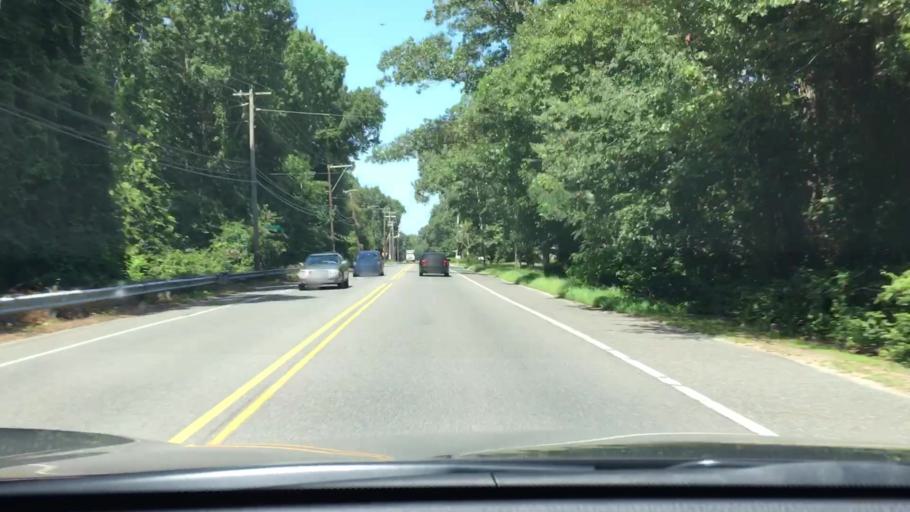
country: US
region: New Jersey
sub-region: Cumberland County
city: Laurel Lake
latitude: 39.3373
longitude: -75.0260
